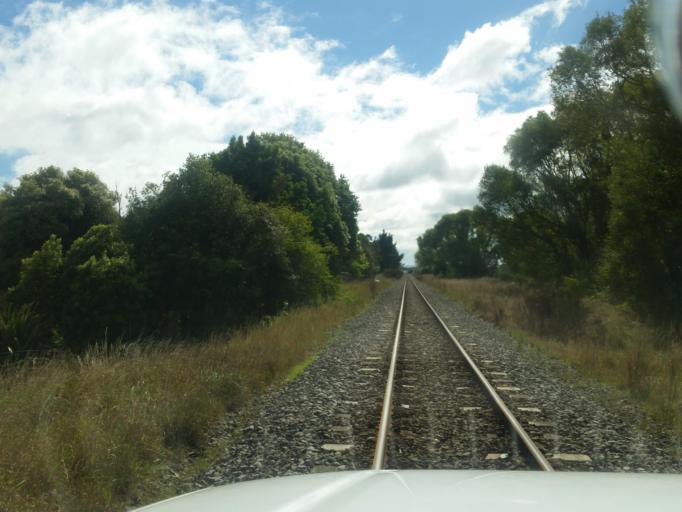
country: NZ
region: Canterbury
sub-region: Waimakariri District
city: Kaiapoi
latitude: -43.3965
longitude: 172.6548
